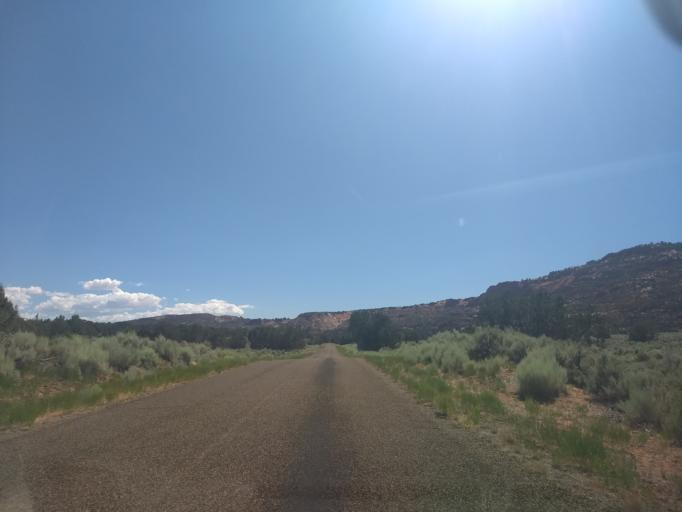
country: US
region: Utah
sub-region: Washington County
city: Hildale
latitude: 37.0071
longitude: -112.8538
